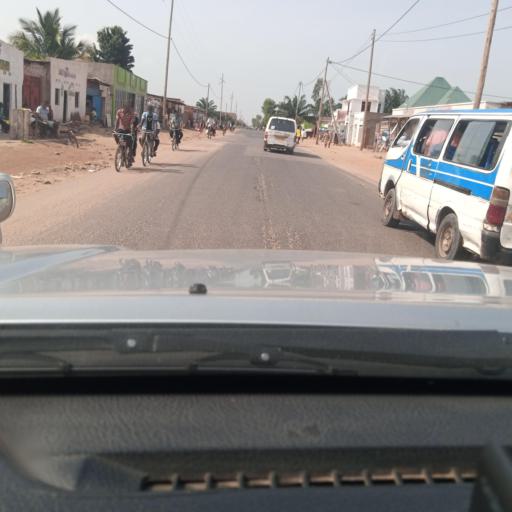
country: BI
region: Bujumbura Mairie
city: Bujumbura
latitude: -3.4537
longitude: 29.3517
